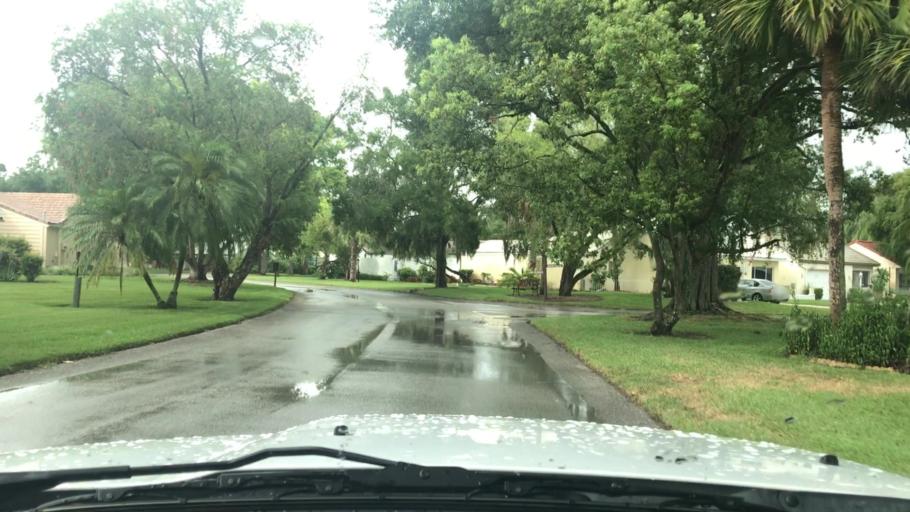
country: US
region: Florida
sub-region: Polk County
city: Cypress Gardens
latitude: 28.0132
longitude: -81.6776
